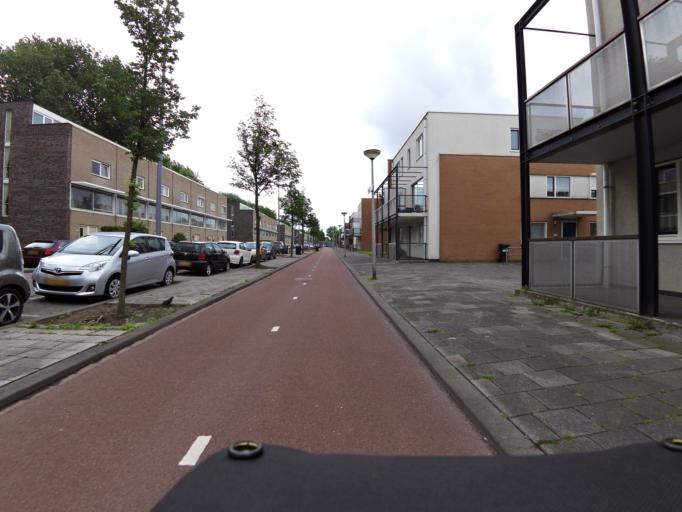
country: NL
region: South Holland
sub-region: Gemeente Spijkenisse
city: Spijkenisse
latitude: 51.8708
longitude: 4.3481
